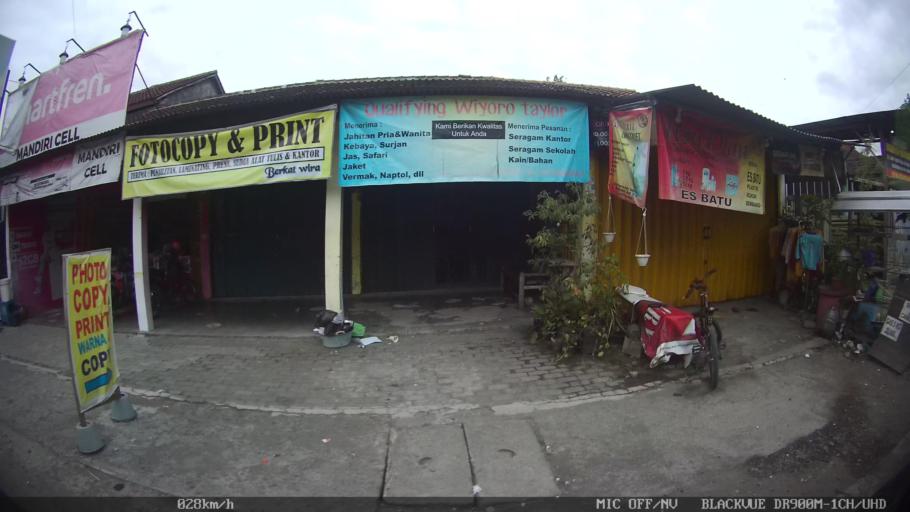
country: ID
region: Daerah Istimewa Yogyakarta
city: Depok
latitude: -7.8270
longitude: 110.4137
